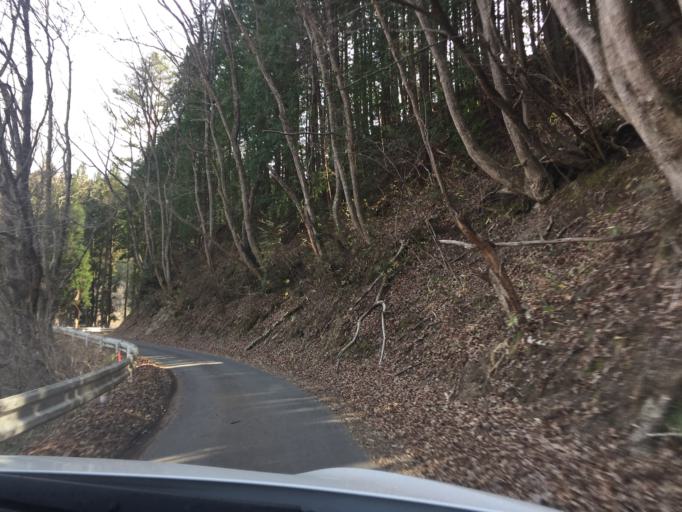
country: JP
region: Fukushima
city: Iwaki
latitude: 37.1281
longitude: 140.7810
